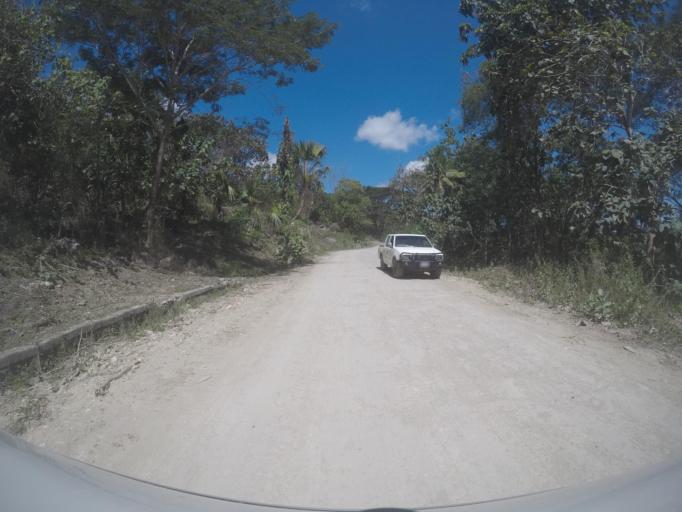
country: TL
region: Viqueque
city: Viqueque
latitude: -8.9086
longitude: 126.3935
